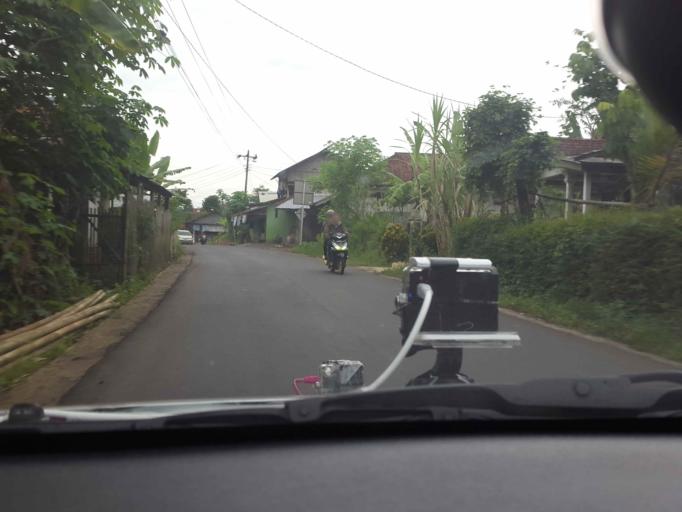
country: ID
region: Central Java
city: Banyumas
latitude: -7.5331
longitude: 109.3130
